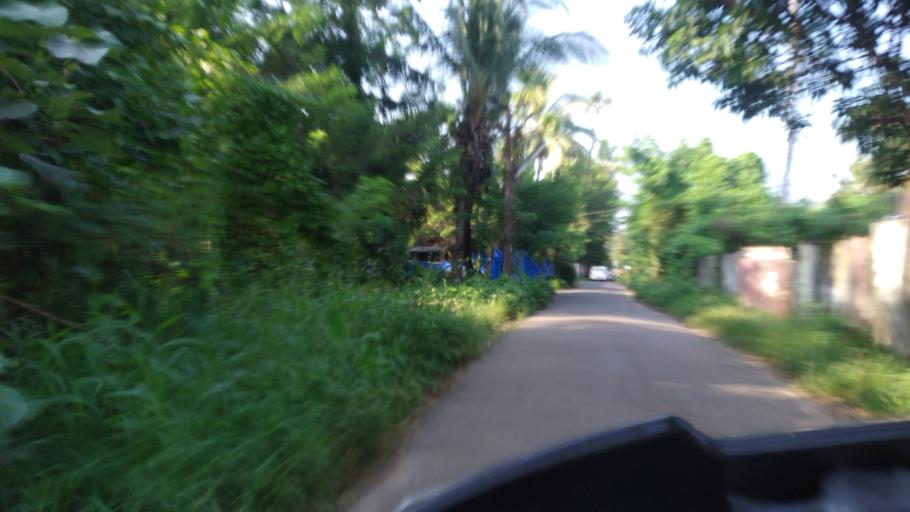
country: IN
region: Kerala
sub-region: Ernakulam
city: Elur
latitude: 10.0431
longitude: 76.2272
